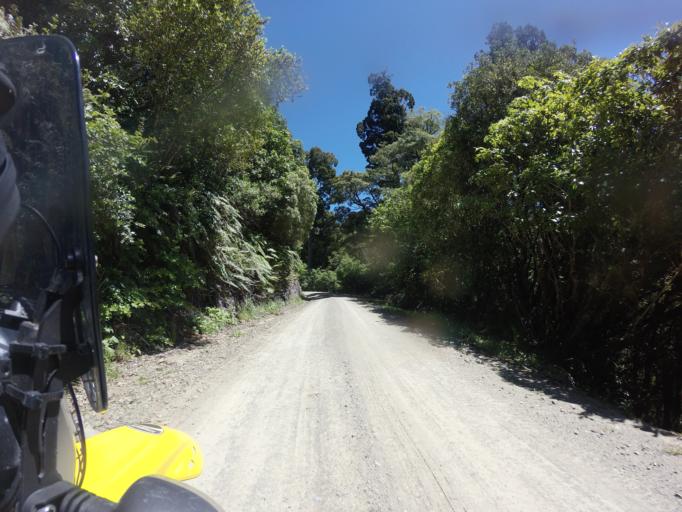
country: NZ
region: Bay of Plenty
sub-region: Opotiki District
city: Opotiki
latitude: -38.4080
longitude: 177.4223
